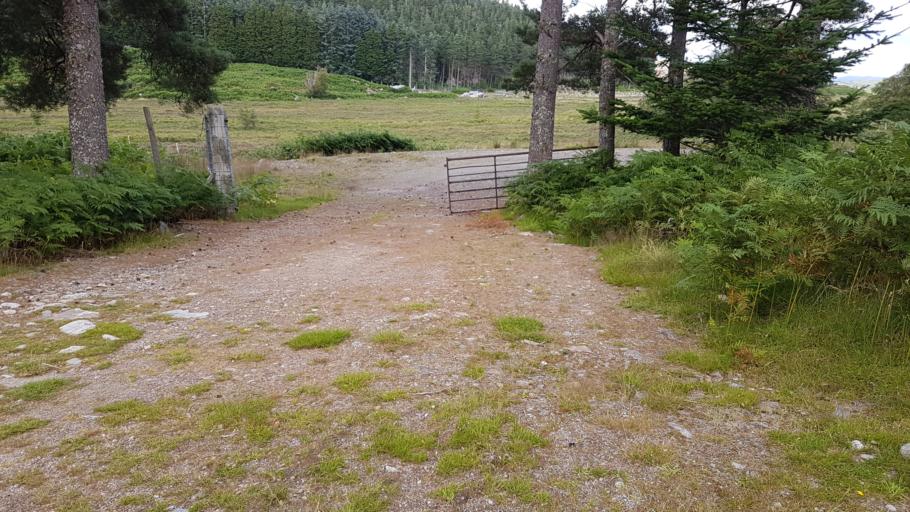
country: GB
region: Scotland
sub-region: Highland
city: Beauly
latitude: 57.2109
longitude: -4.5187
